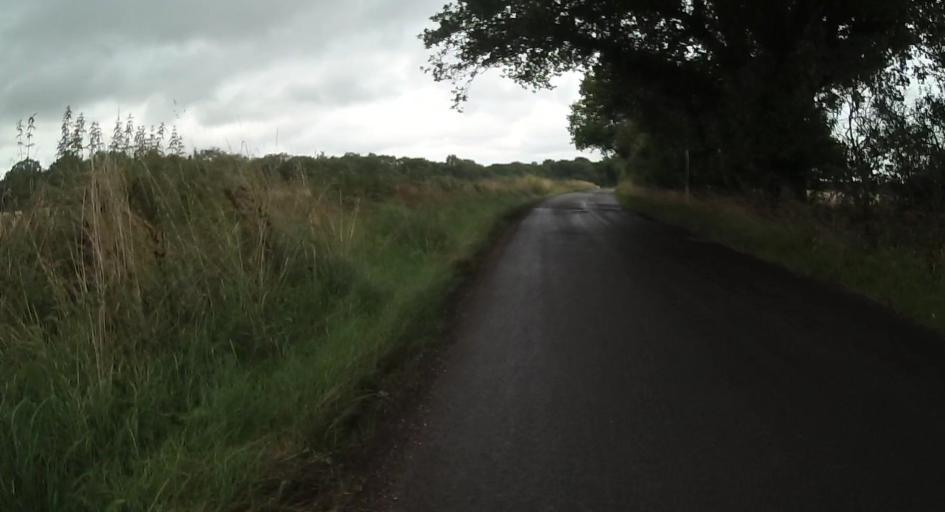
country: GB
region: England
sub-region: Hampshire
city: Andover
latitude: 51.2019
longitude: -1.4174
